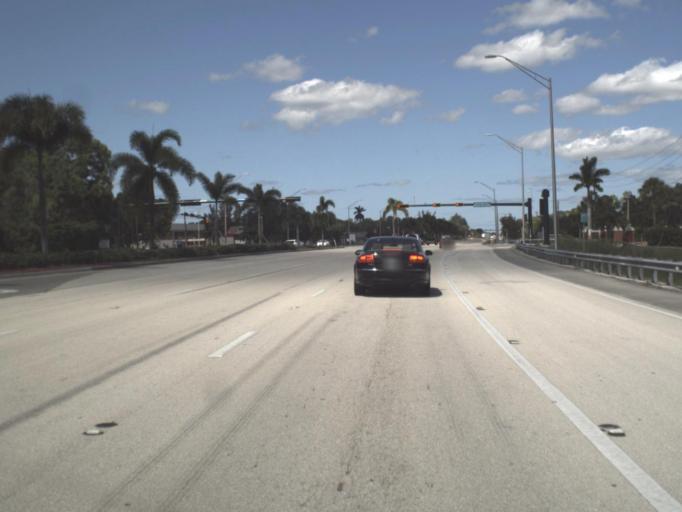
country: US
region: Florida
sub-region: Collier County
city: Naples Manor
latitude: 26.0770
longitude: -81.7202
